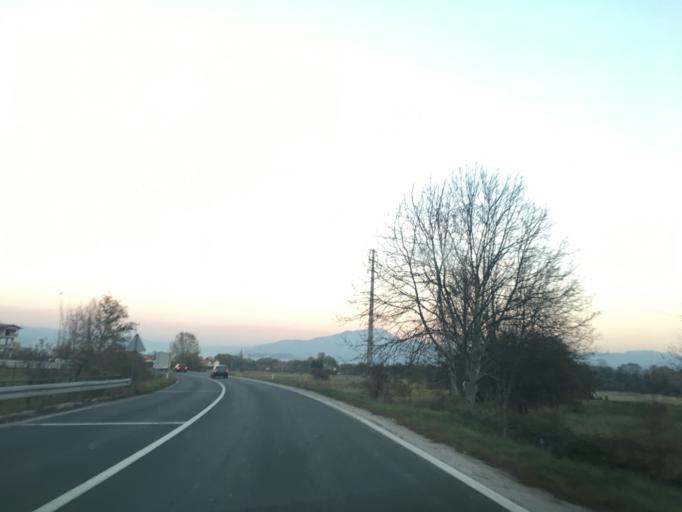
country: BA
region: Federation of Bosnia and Herzegovina
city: Hadzici
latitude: 43.8304
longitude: 18.2735
